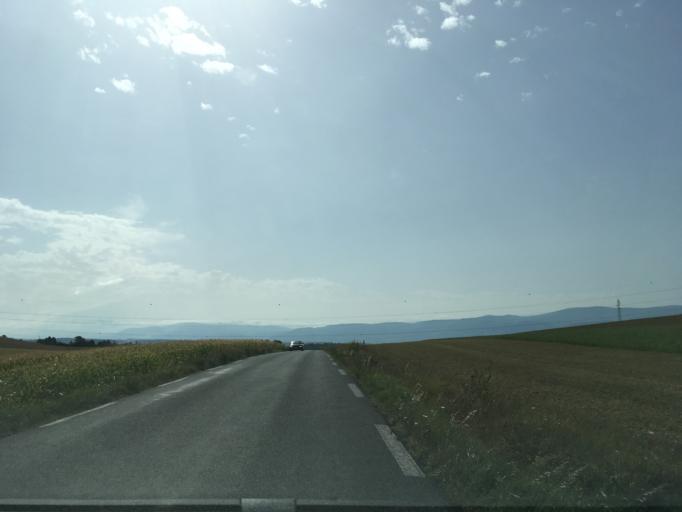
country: FR
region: Midi-Pyrenees
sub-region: Departement du Tarn
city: Lagarrigue
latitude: 43.5822
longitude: 2.2634
